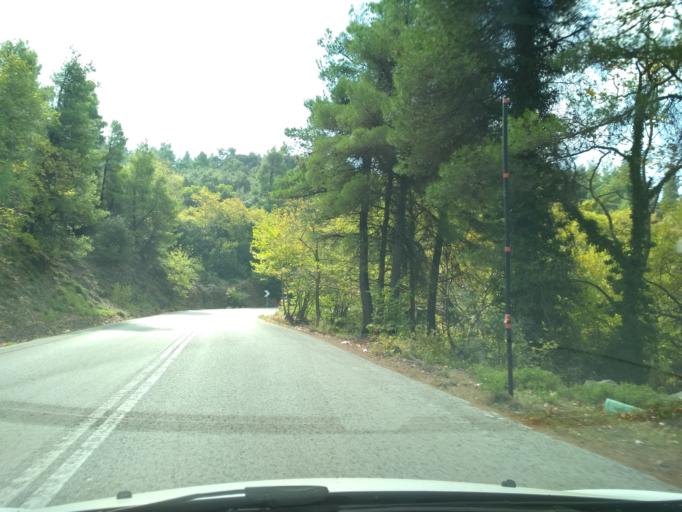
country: GR
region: Central Greece
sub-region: Nomos Evvoias
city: Politika
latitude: 38.6678
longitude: 23.5580
